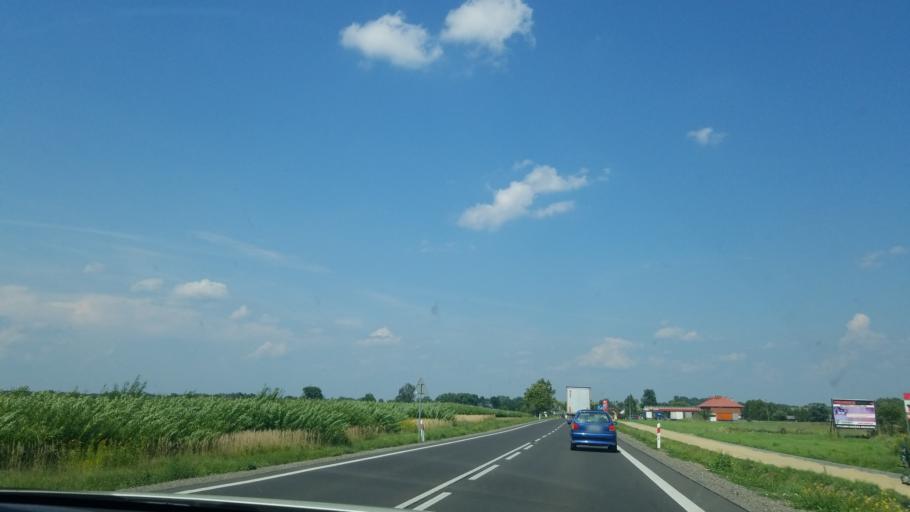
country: PL
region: Subcarpathian Voivodeship
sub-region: Powiat nizanski
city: Jezowe
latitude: 50.3657
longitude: 22.1247
